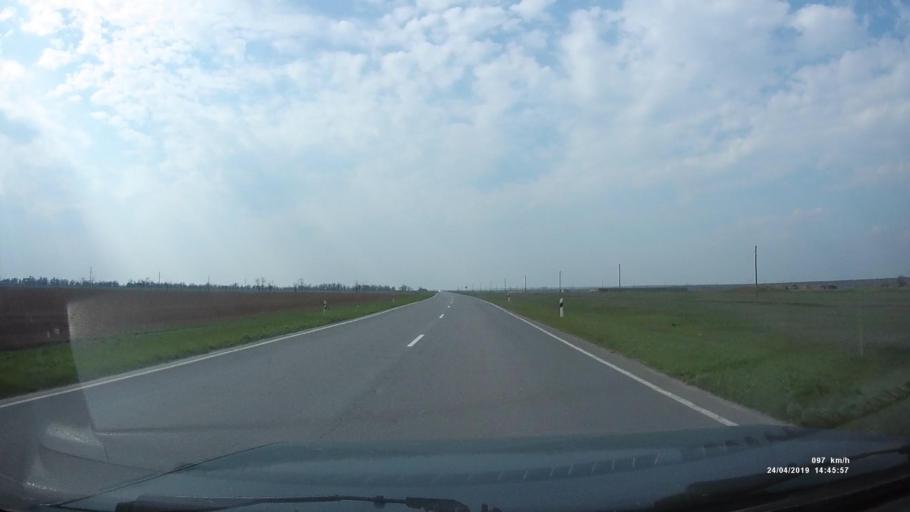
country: RU
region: Rostov
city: Remontnoye
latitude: 46.4775
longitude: 43.7985
